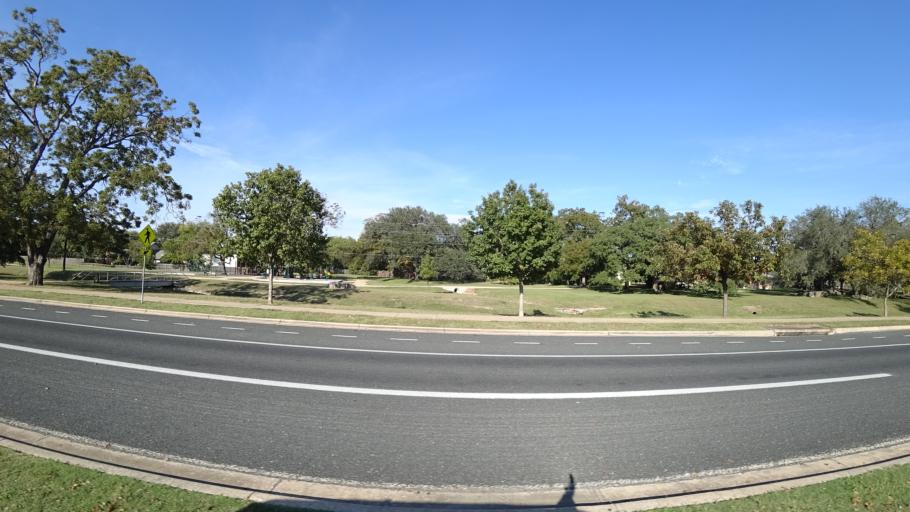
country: US
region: Texas
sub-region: Williamson County
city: Anderson Mill
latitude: 30.4584
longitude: -97.8111
